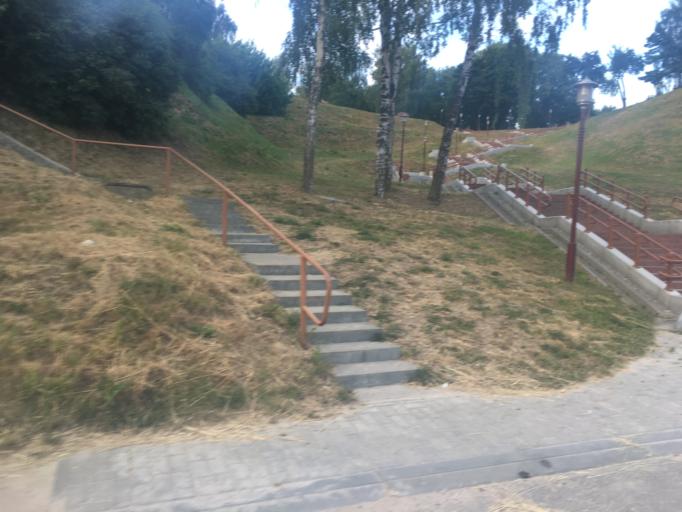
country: BY
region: Grodnenskaya
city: Hrodna
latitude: 53.6784
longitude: 23.8169
